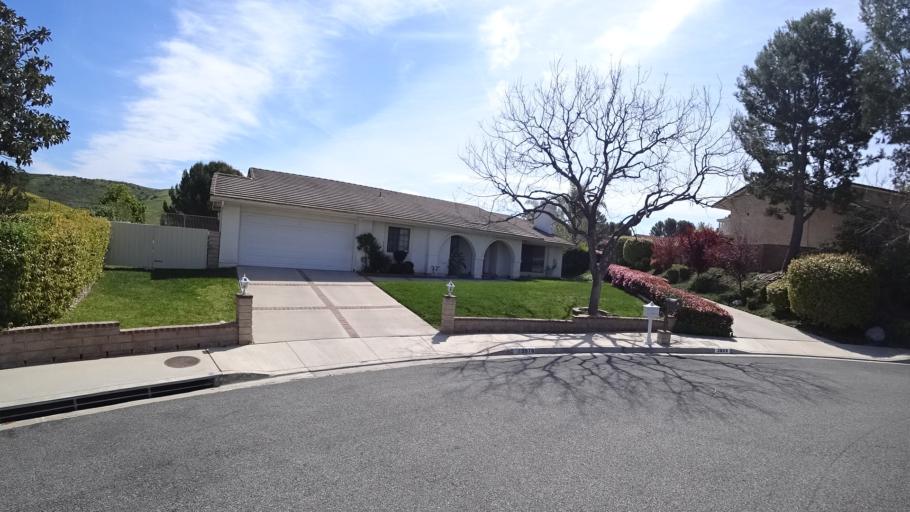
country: US
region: California
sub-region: Ventura County
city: Thousand Oaks
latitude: 34.2322
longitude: -118.8427
